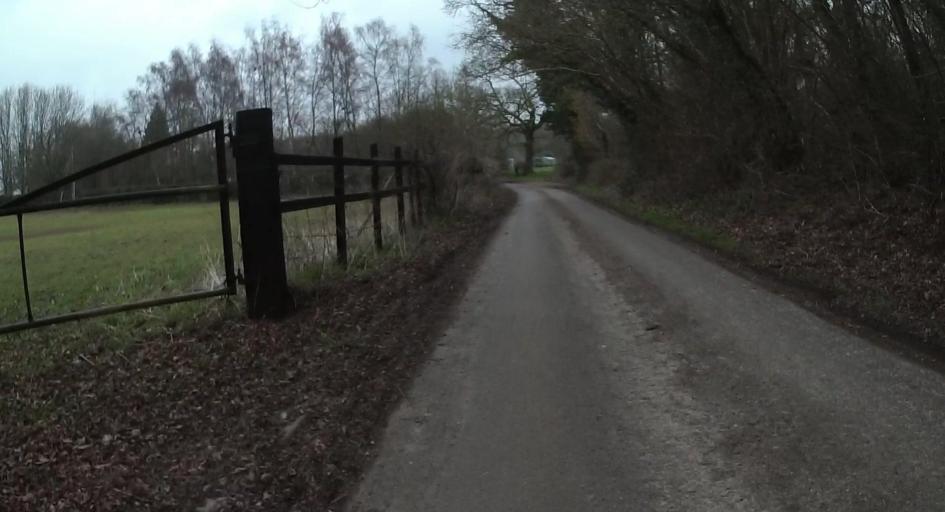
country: GB
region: England
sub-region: Hampshire
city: Four Marks
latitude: 51.0970
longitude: -1.1063
